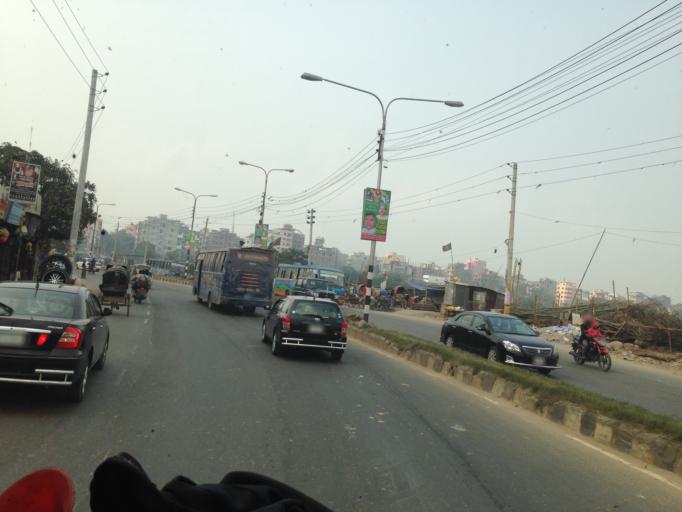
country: BD
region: Dhaka
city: Tungi
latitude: 23.8233
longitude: 90.3803
